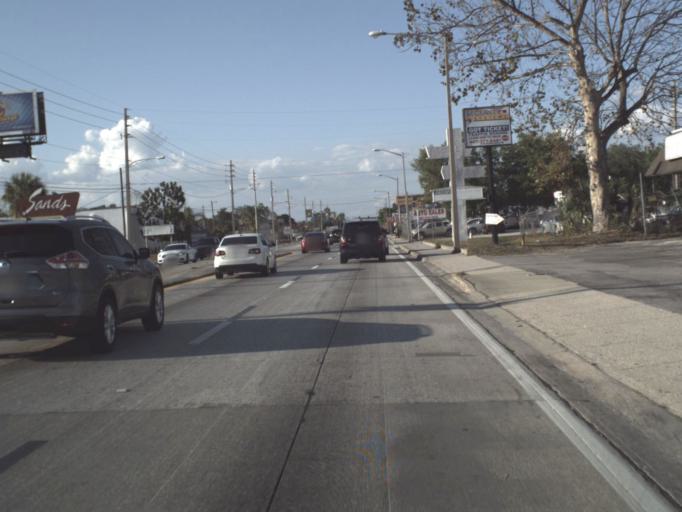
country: US
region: Florida
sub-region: Orange County
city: Holden Heights
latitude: 28.5165
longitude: -81.3969
